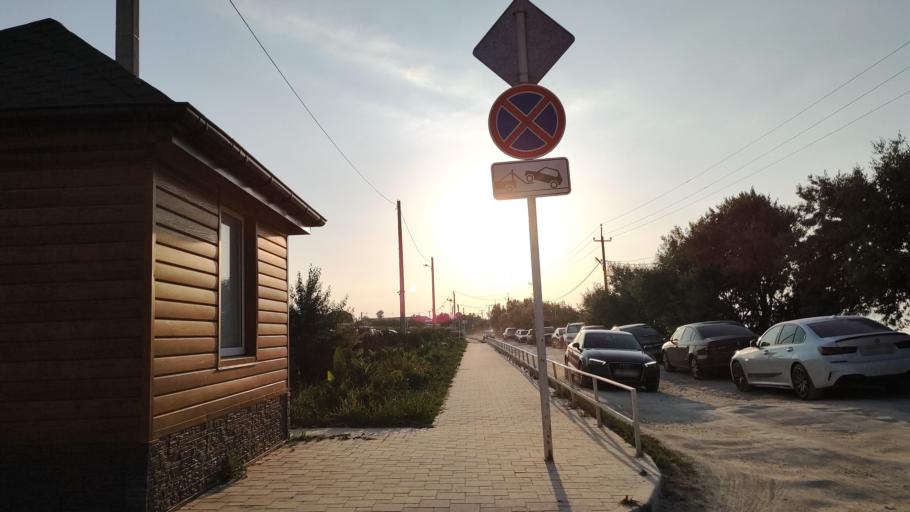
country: RU
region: Krasnodarskiy
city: Blagovetschenskaya
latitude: 45.0656
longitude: 37.0444
